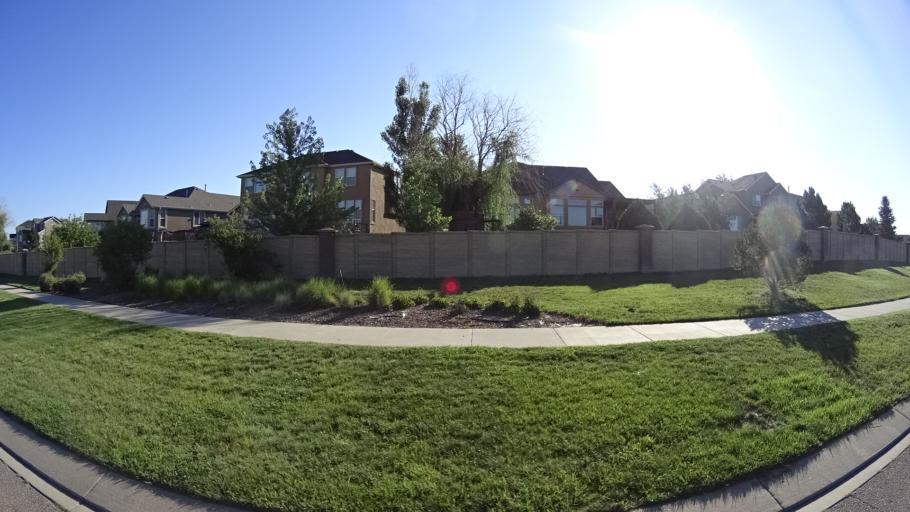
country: US
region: Colorado
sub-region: El Paso County
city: Black Forest
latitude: 38.9841
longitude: -104.7732
